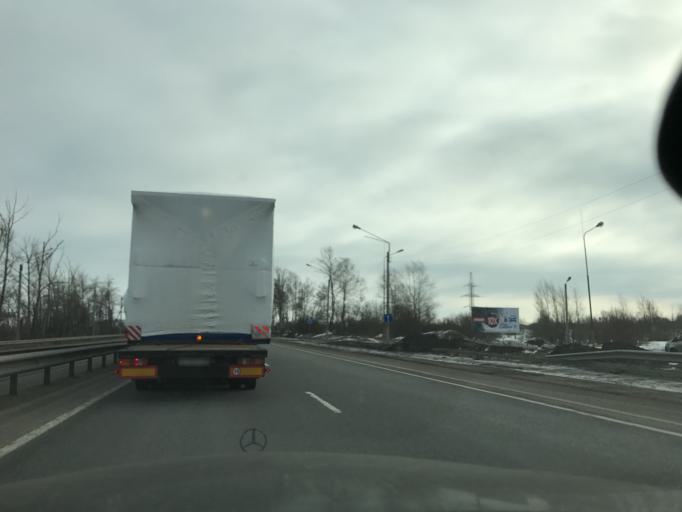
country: RU
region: Vladimir
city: Vyazniki
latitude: 56.2395
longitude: 42.0848
